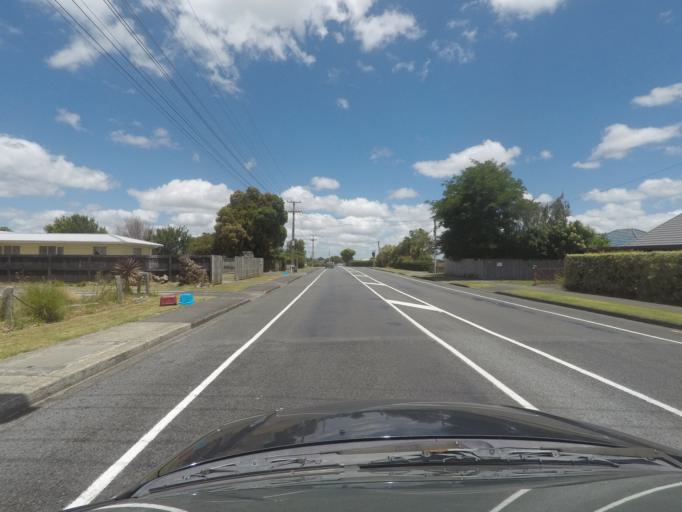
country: NZ
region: Northland
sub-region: Whangarei
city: Whangarei
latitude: -35.7590
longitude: 174.3673
